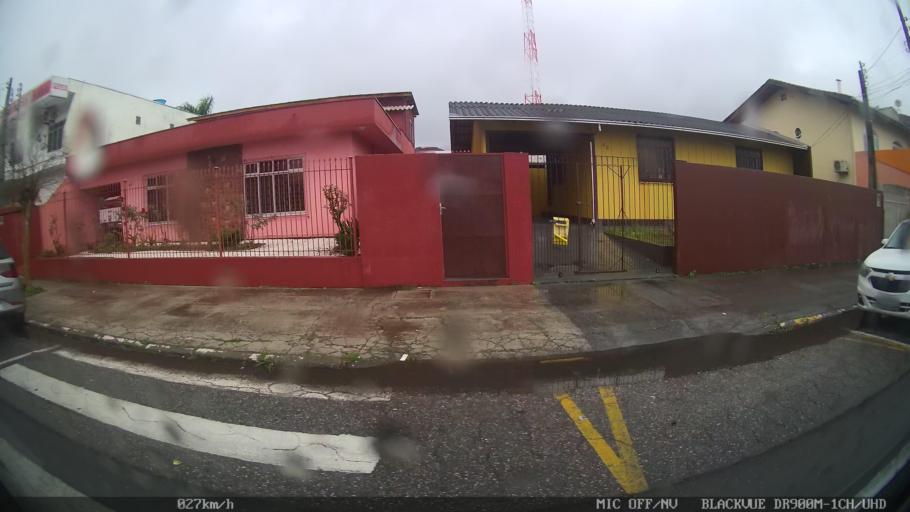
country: BR
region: Santa Catarina
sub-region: Itajai
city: Itajai
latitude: -26.9207
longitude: -48.6772
